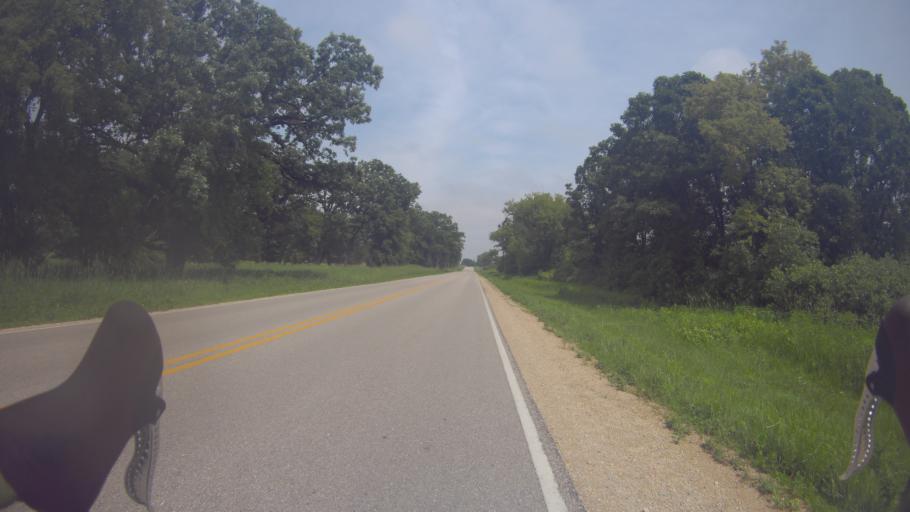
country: US
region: Wisconsin
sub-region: Rock County
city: Edgerton
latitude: 42.8692
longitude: -89.0341
